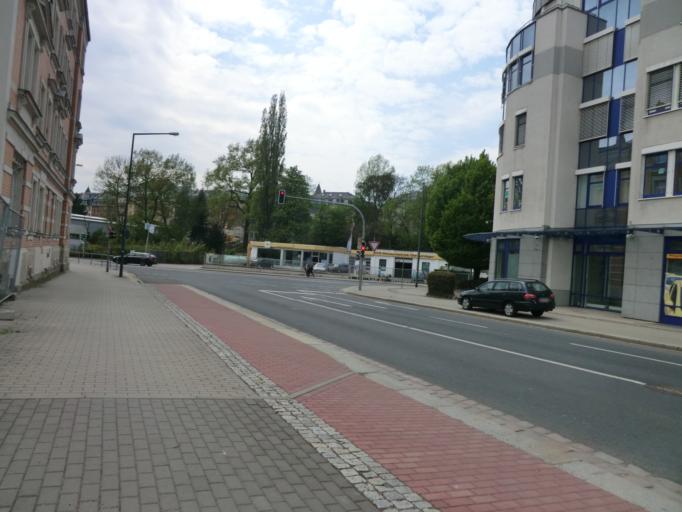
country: DE
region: Saxony
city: Dresden
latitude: 51.0405
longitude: 13.7052
